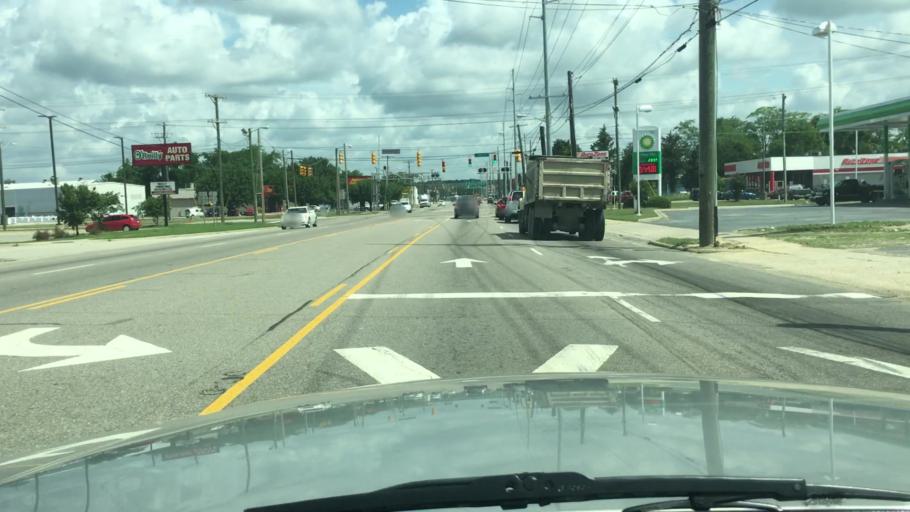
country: US
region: North Carolina
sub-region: Cumberland County
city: Fayetteville
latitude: 35.0451
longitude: -78.8657
